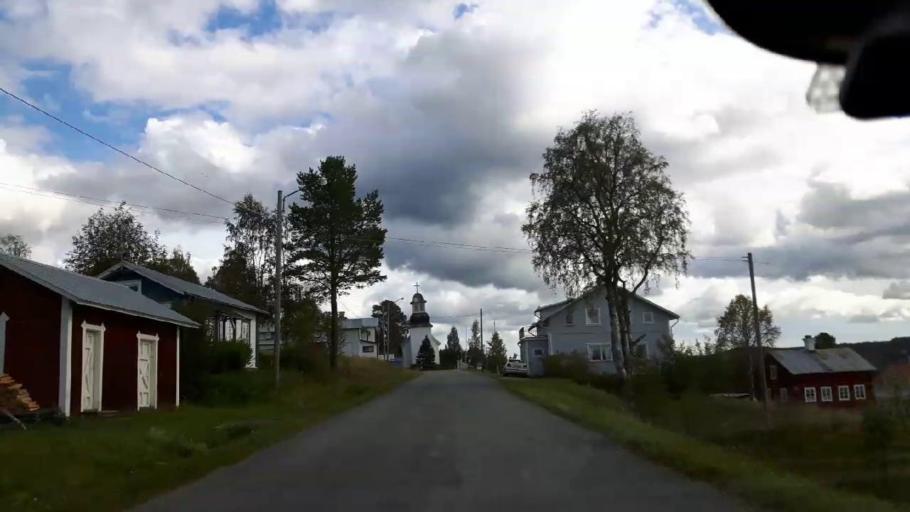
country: SE
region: Jaemtland
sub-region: Stroemsunds Kommun
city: Stroemsund
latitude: 63.4238
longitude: 15.8236
